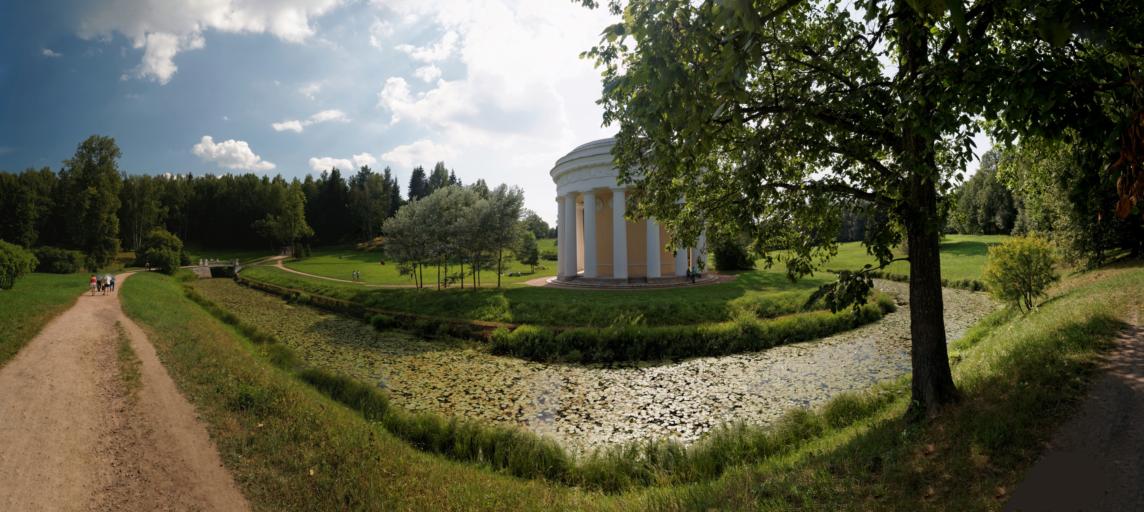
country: RU
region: St.-Petersburg
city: Tyarlevo
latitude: 59.6886
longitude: 30.4562
